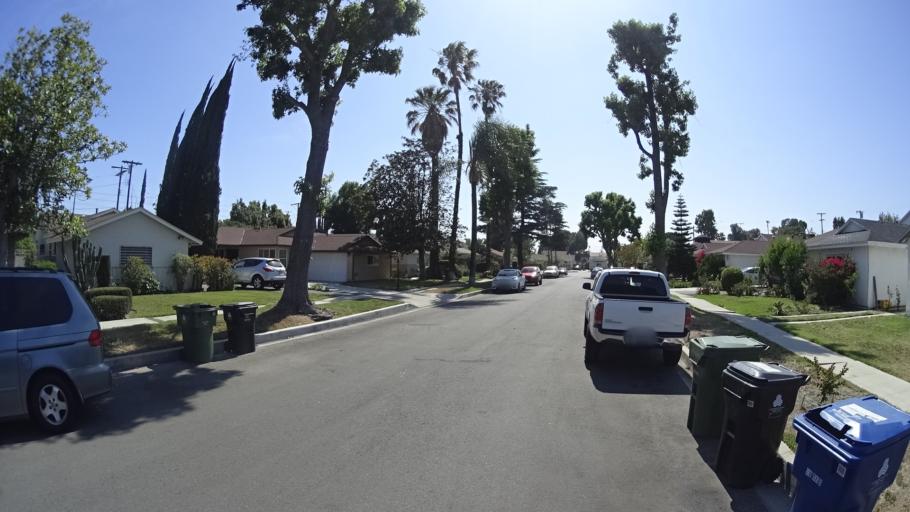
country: US
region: California
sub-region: Los Angeles County
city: Van Nuys
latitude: 34.1948
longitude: -118.4192
